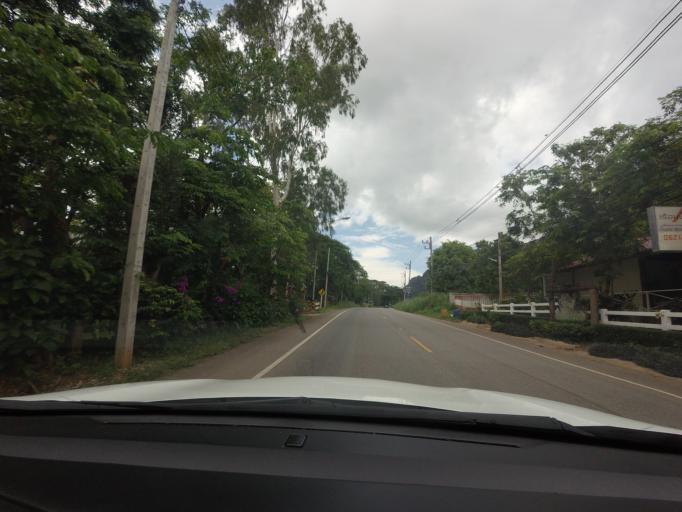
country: TH
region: Sara Buri
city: Muak Lek
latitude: 14.5461
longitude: 101.3288
